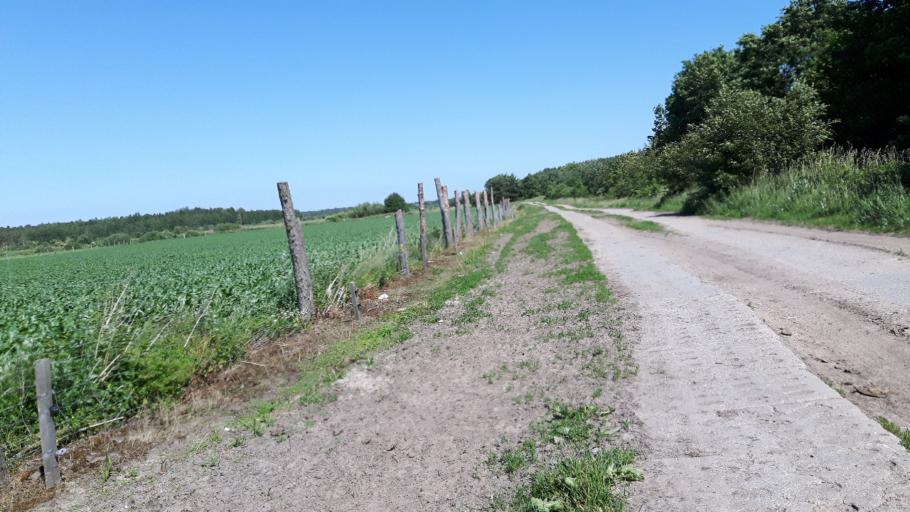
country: PL
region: Pomeranian Voivodeship
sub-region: Powiat slupski
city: Glowczyce
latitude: 54.6409
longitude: 17.3819
